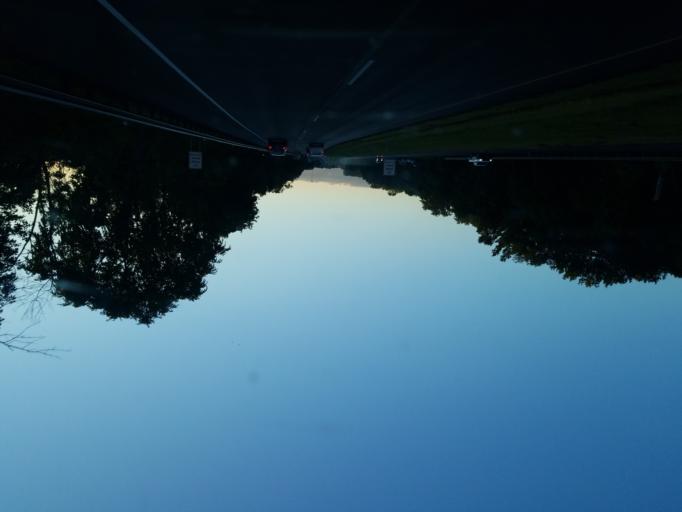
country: US
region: Ohio
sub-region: Summit County
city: Norton
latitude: 41.0861
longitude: -81.6614
